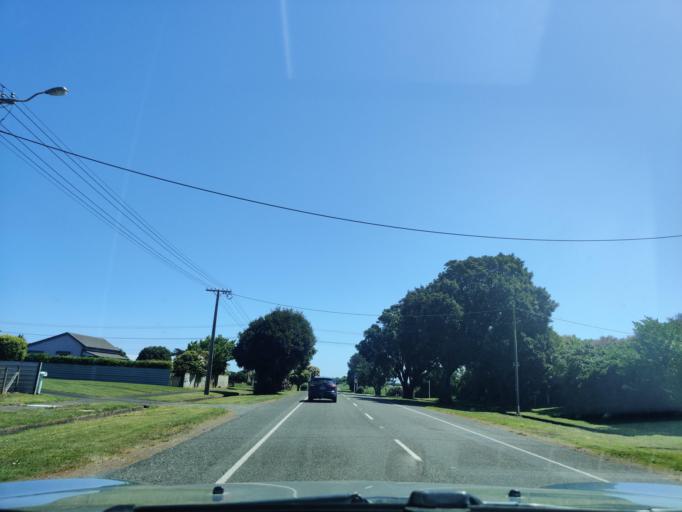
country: NZ
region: Taranaki
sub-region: South Taranaki District
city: Hawera
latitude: -39.5504
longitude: 174.1198
